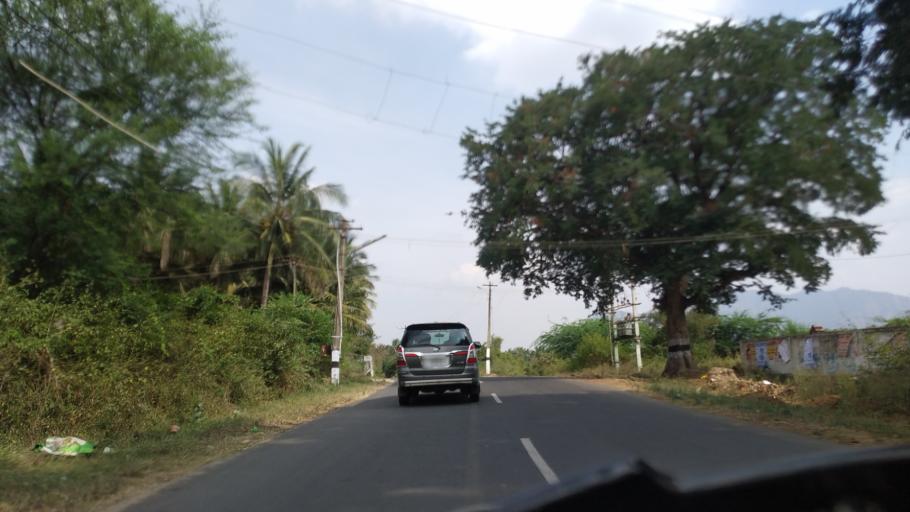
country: IN
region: Tamil Nadu
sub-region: Coimbatore
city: Perur
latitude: 10.9503
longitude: 76.7664
